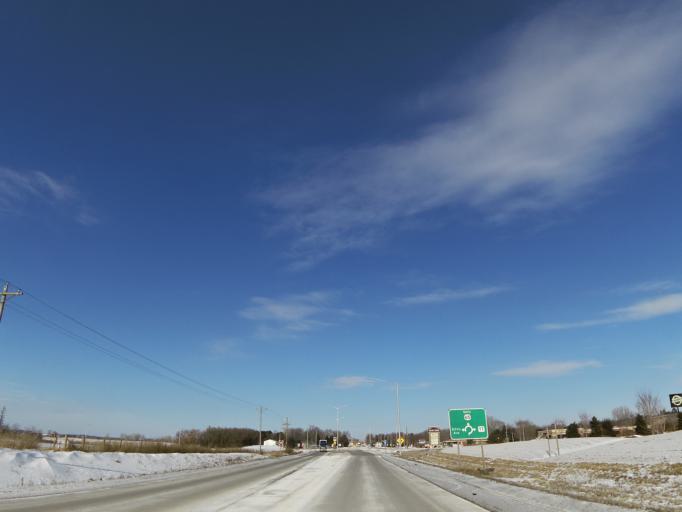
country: US
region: Wisconsin
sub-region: Saint Croix County
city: Roberts
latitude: 44.9755
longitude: -92.5581
